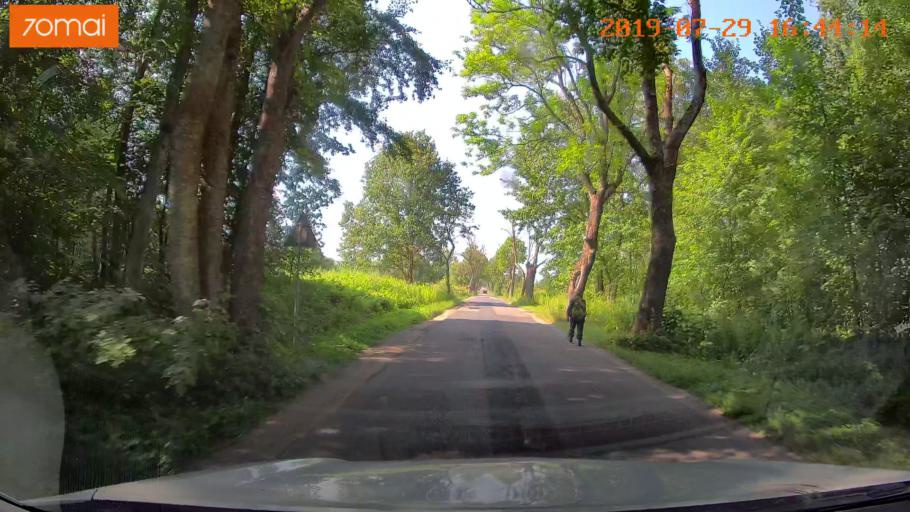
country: RU
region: Kaliningrad
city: Primorsk
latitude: 54.7537
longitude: 20.0889
